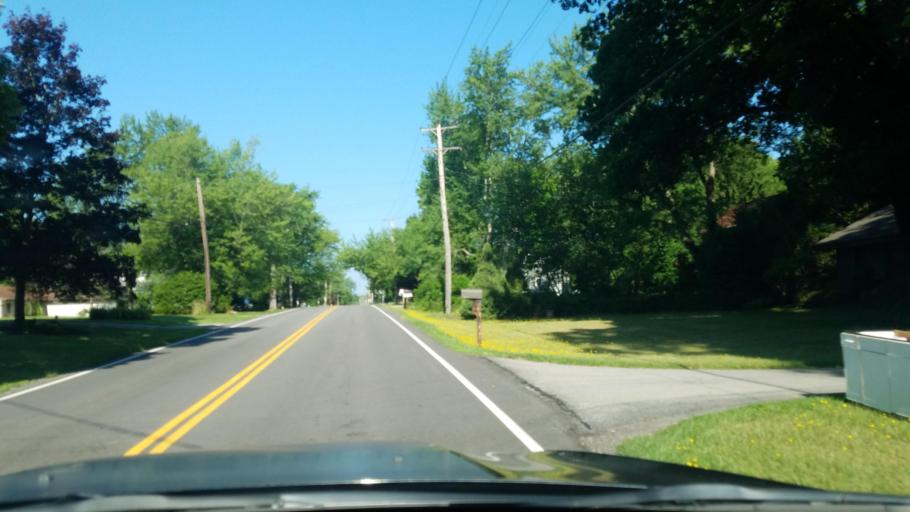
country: US
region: Ohio
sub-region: Trumbull County
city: Champion Heights
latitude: 41.2916
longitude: -80.8336
